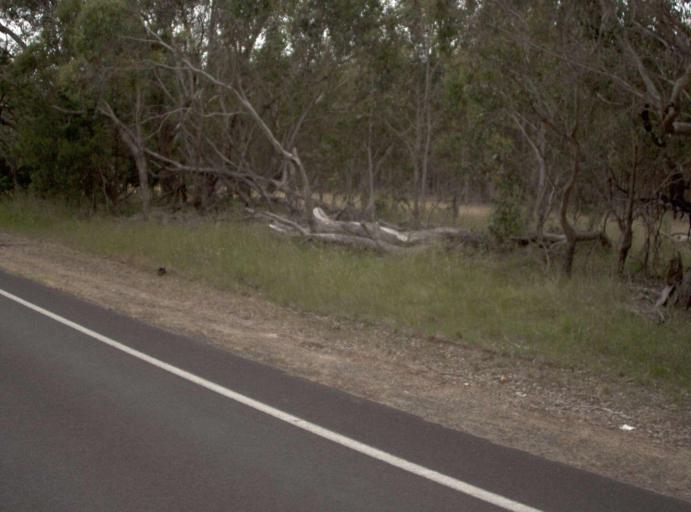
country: AU
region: Victoria
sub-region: Wellington
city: Sale
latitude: -38.4218
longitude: 146.9573
